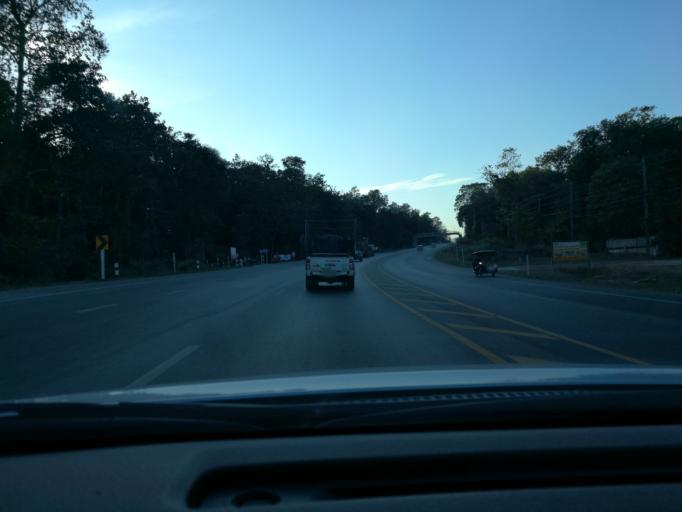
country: TH
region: Phitsanulok
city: Wang Thong
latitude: 16.8433
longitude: 100.5333
